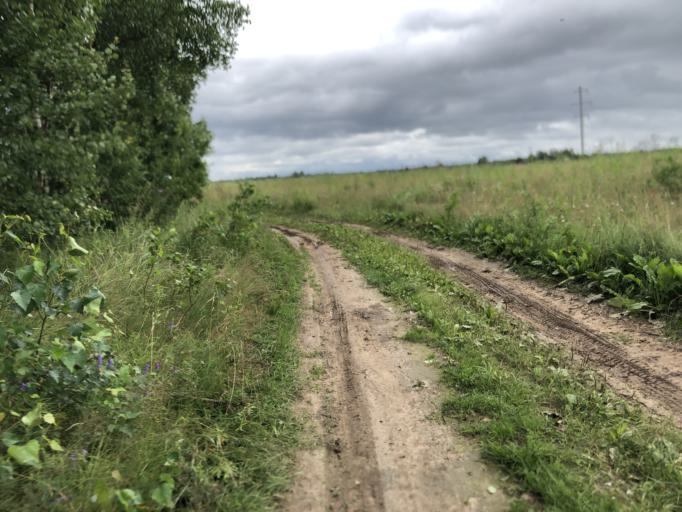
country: RU
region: Tverskaya
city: Rzhev
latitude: 56.2403
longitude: 34.3791
